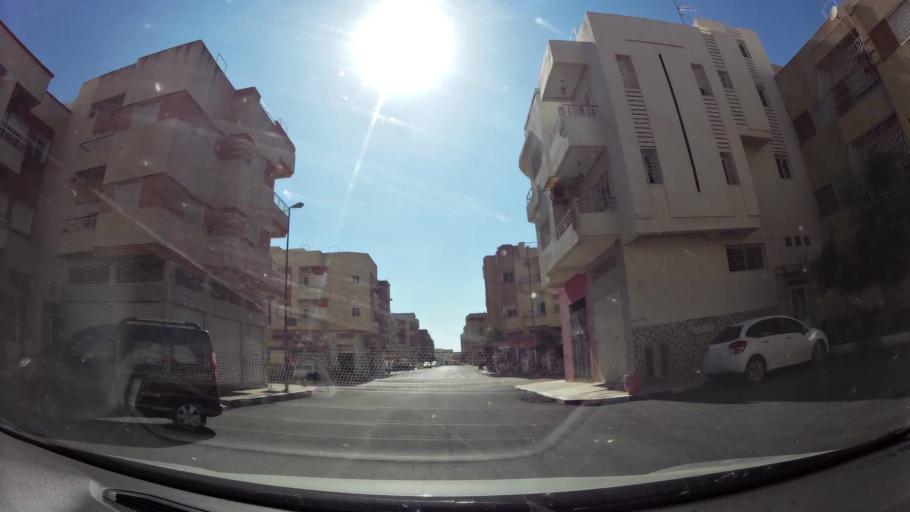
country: MA
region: Fes-Boulemane
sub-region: Fes
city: Fes
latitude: 34.0001
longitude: -5.0051
